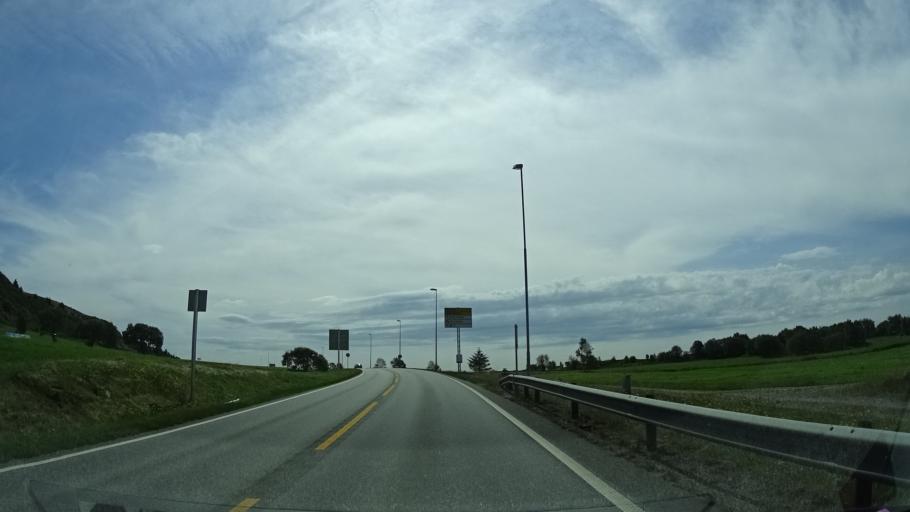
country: NO
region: Rogaland
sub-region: Rennesoy
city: Vikevag
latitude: 59.0678
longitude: 5.6731
